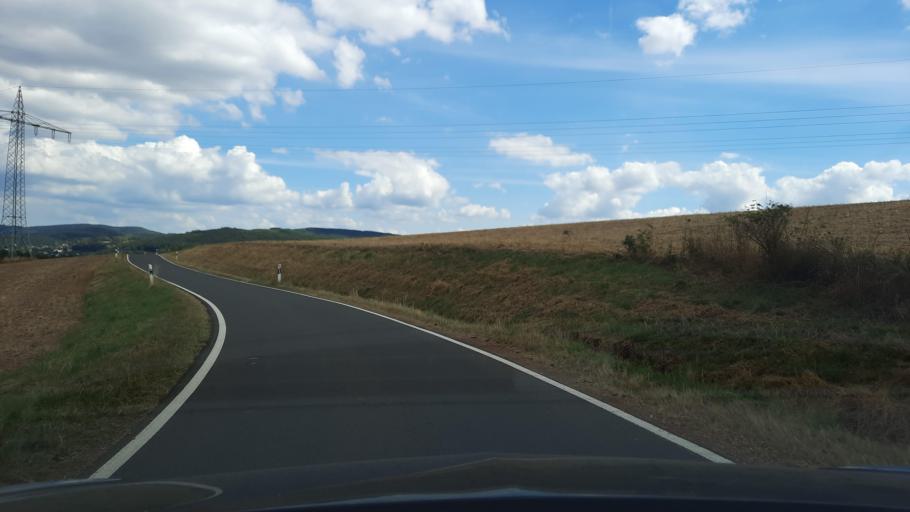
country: DE
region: Rheinland-Pfalz
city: Pronsfeld
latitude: 50.1791
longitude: 6.3284
